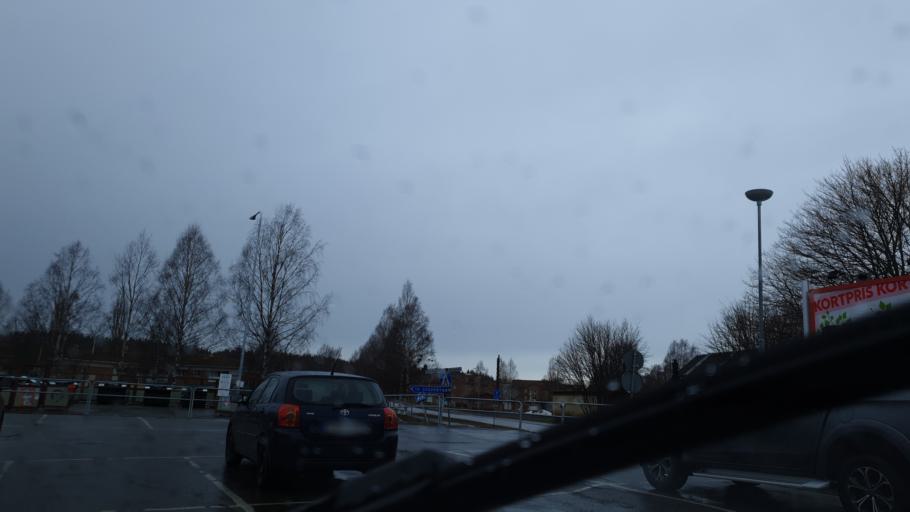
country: SE
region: Vaesterbotten
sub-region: Skelleftea Kommun
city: Kage
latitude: 64.8322
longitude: 20.9875
